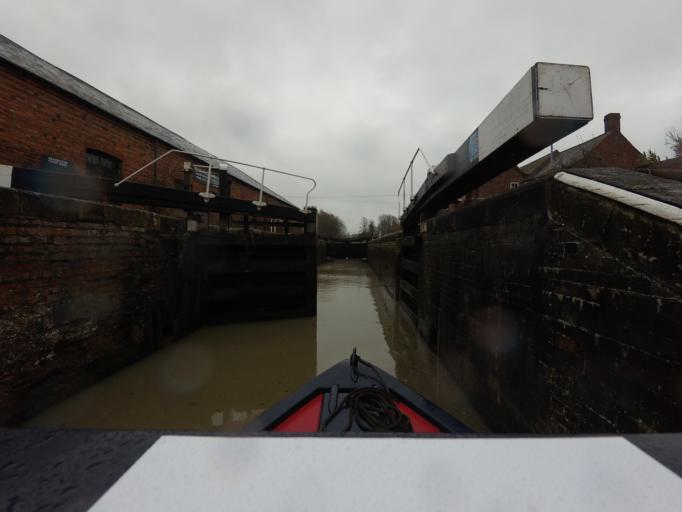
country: GB
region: England
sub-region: Northamptonshire
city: Daventry
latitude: 52.2891
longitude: -1.2030
